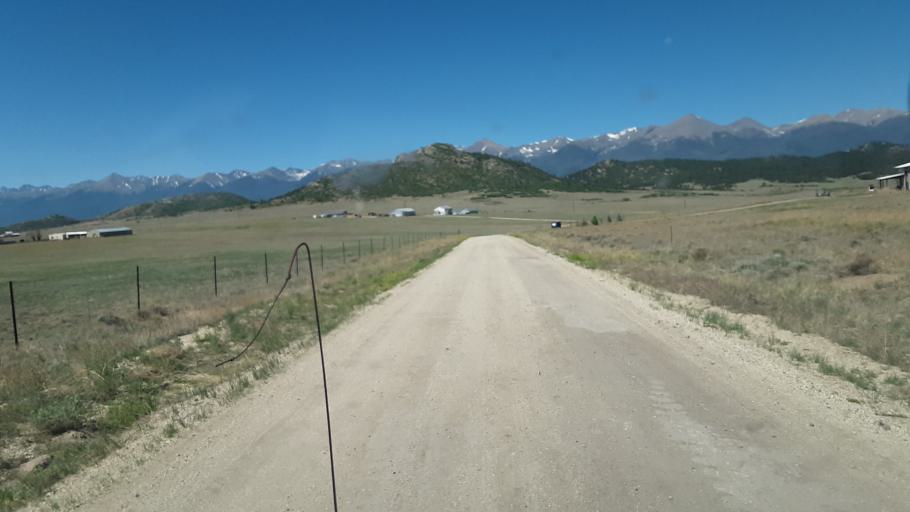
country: US
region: Colorado
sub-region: Custer County
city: Westcliffe
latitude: 38.2365
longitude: -105.4946
